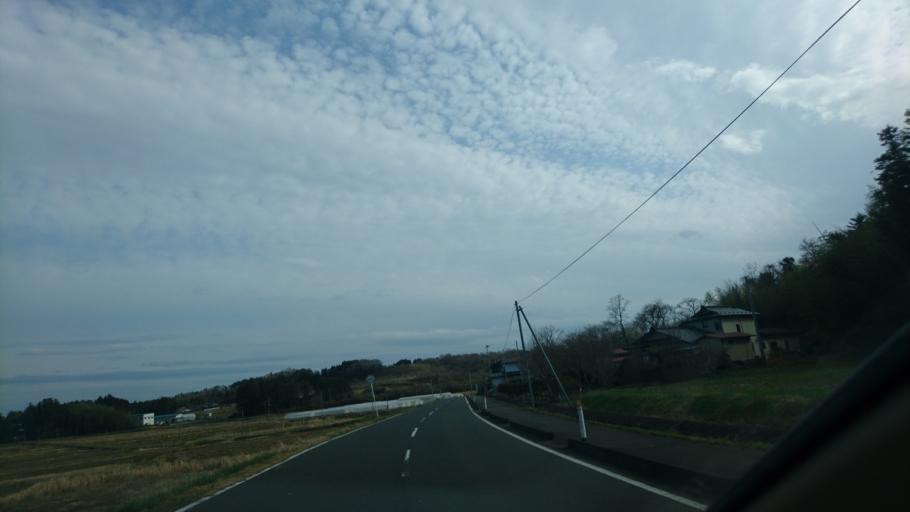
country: JP
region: Iwate
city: Ichinoseki
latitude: 38.8094
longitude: 141.0310
